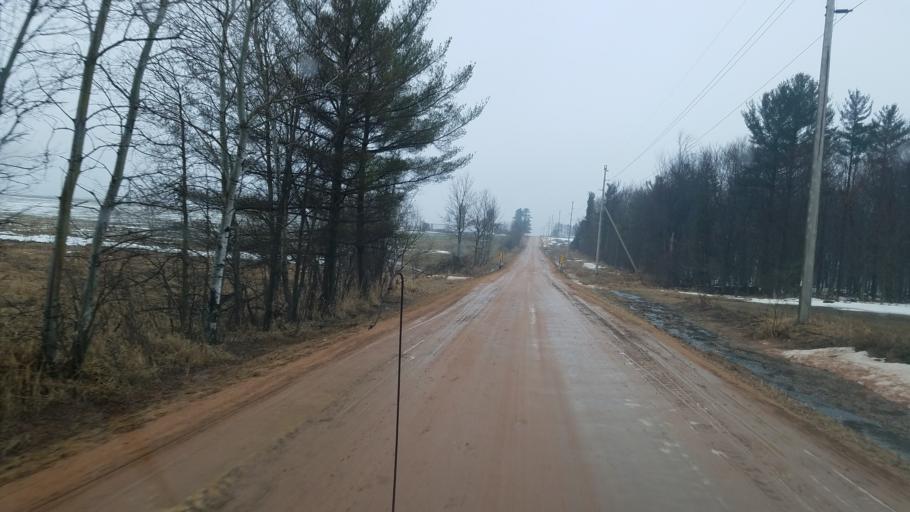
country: US
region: Wisconsin
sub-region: Clark County
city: Loyal
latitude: 44.5887
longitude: -90.3957
